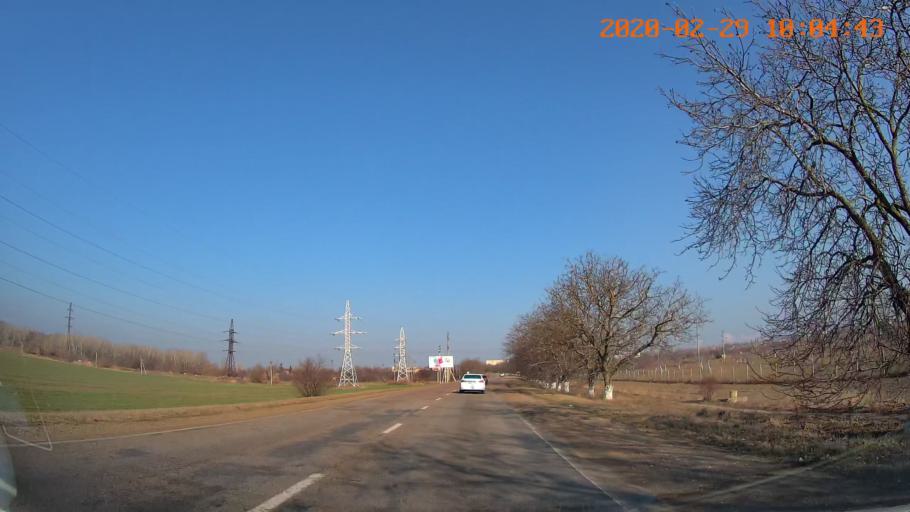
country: MD
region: Causeni
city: Chitcani
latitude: 46.8005
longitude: 29.6744
